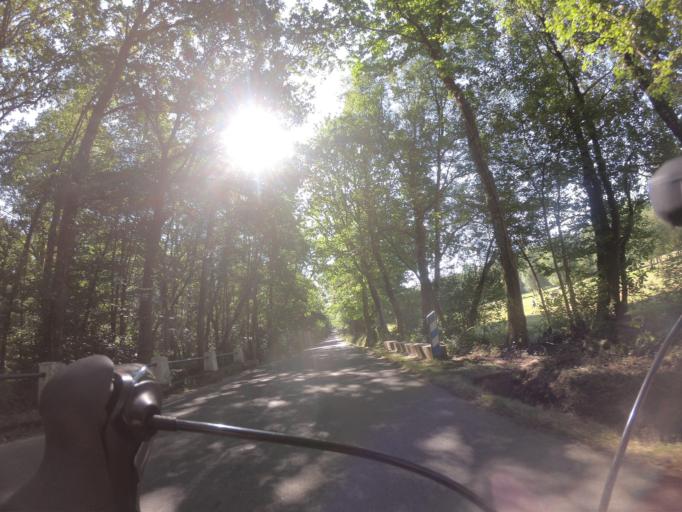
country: FR
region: Lower Normandy
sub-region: Departement de l'Orne
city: Tesse-la-Madeleine
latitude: 48.5637
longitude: -0.4321
